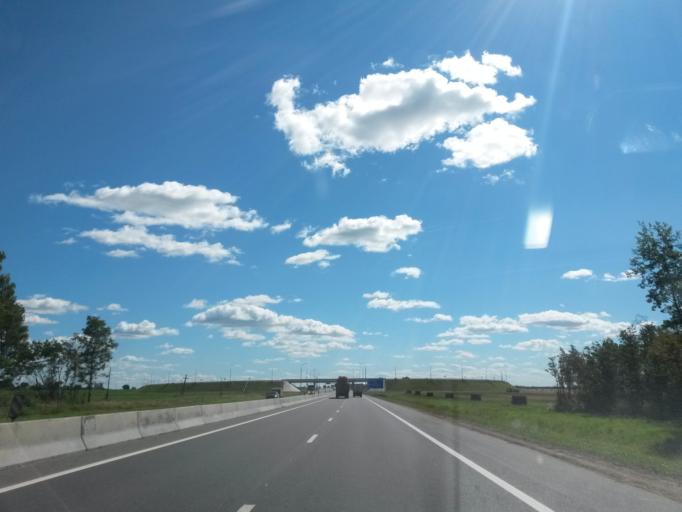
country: RU
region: Jaroslavl
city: Yaroslavl
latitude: 57.7277
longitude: 39.8990
